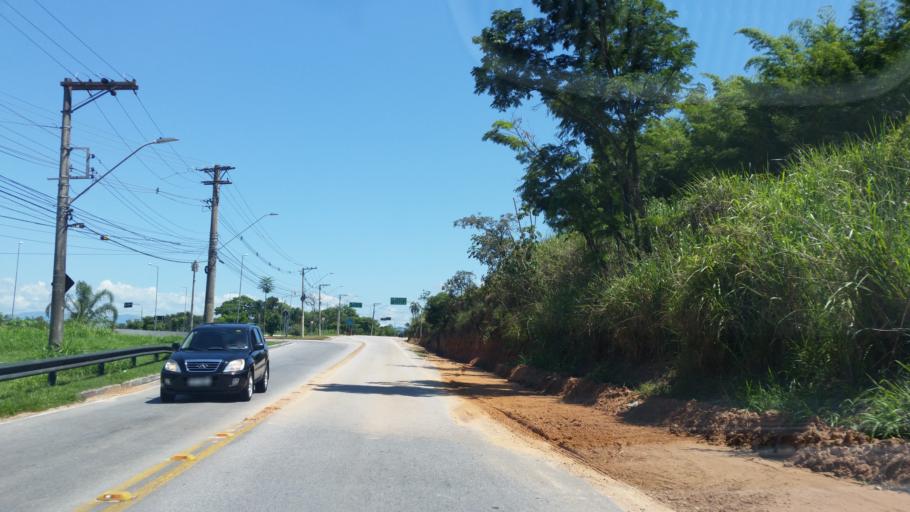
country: BR
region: Sao Paulo
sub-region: Sao Jose Dos Campos
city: Sao Jose dos Campos
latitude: -23.1595
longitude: -45.8041
